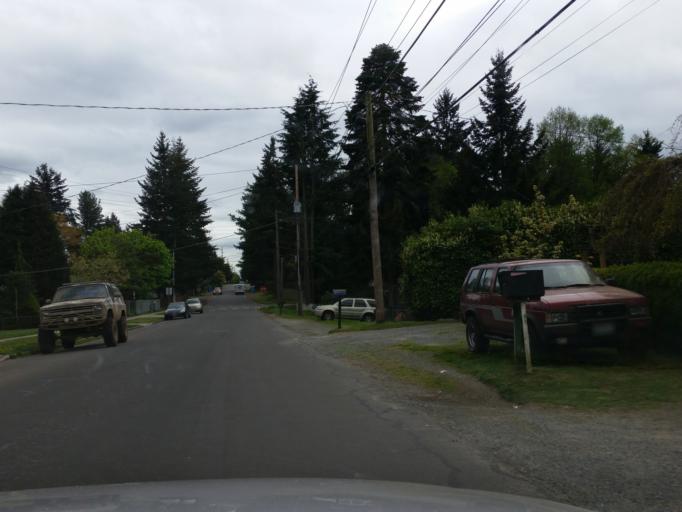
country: US
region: Washington
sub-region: King County
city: Shoreline
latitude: 47.7642
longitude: -122.3217
